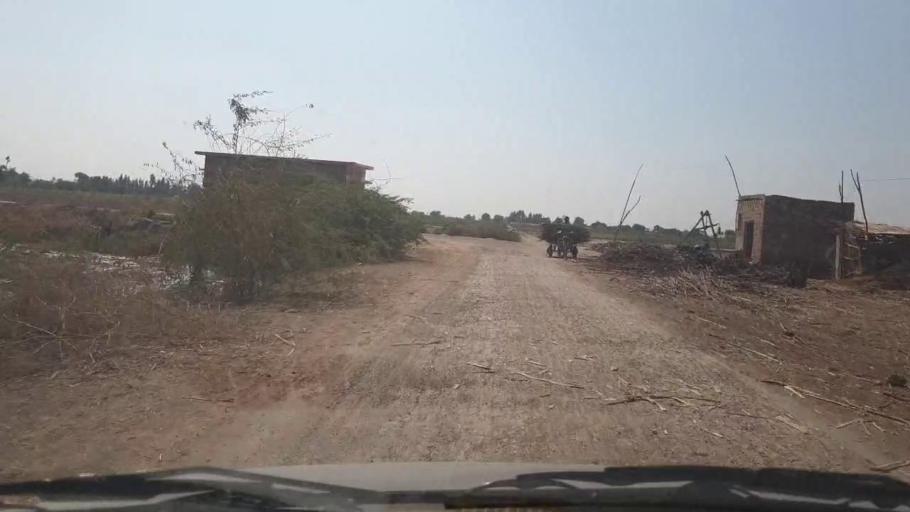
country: PK
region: Sindh
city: Samaro
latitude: 25.2230
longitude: 69.3325
